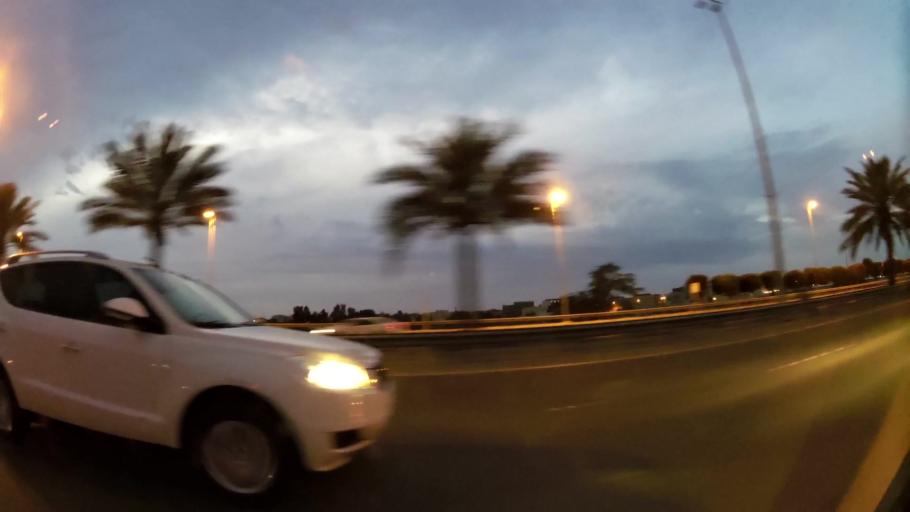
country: BH
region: Northern
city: Madinat `Isa
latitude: 26.1943
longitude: 50.5066
